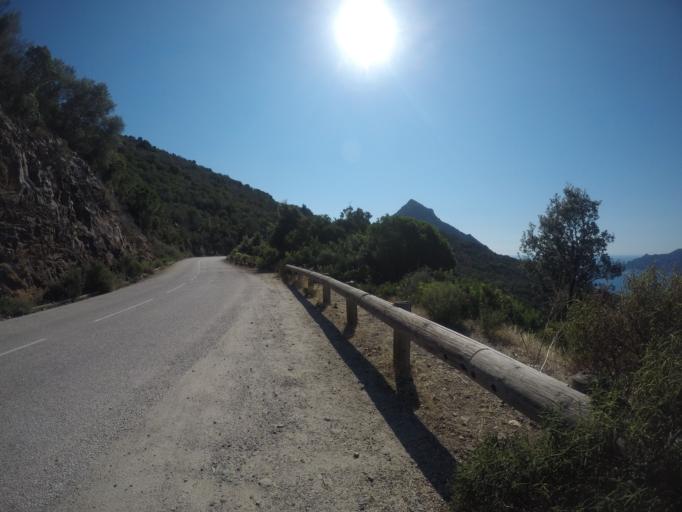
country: FR
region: Corsica
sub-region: Departement de la Corse-du-Sud
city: Cargese
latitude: 42.3286
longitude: 8.6358
